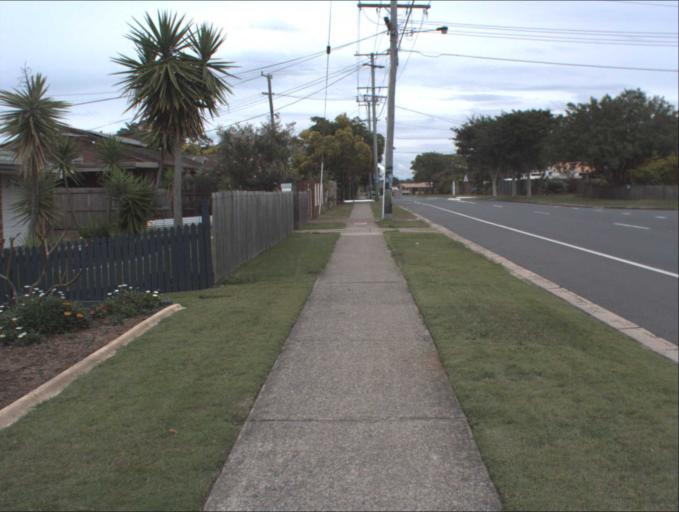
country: AU
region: Queensland
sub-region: Brisbane
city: Sunnybank Hills
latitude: -27.6626
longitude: 153.0227
